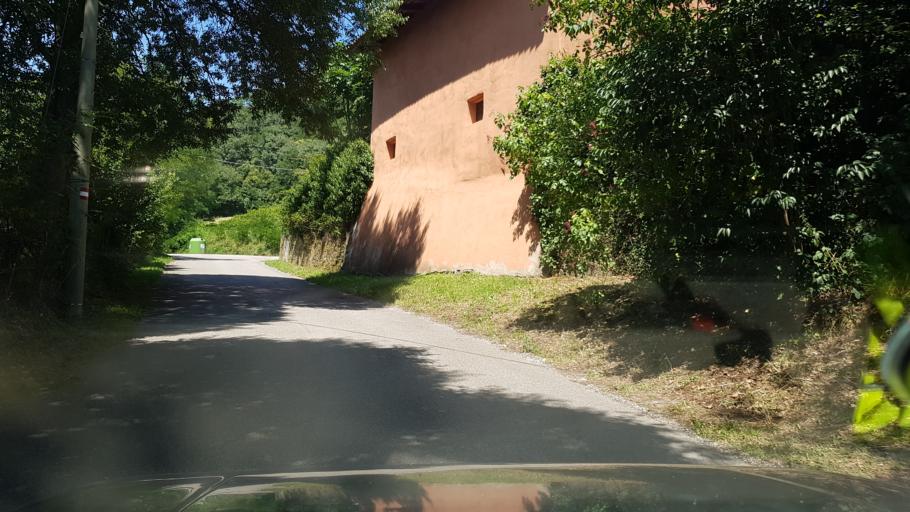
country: IT
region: Friuli Venezia Giulia
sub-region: Provincia di Gorizia
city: Farra d'Isonzo
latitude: 45.9054
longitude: 13.5411
